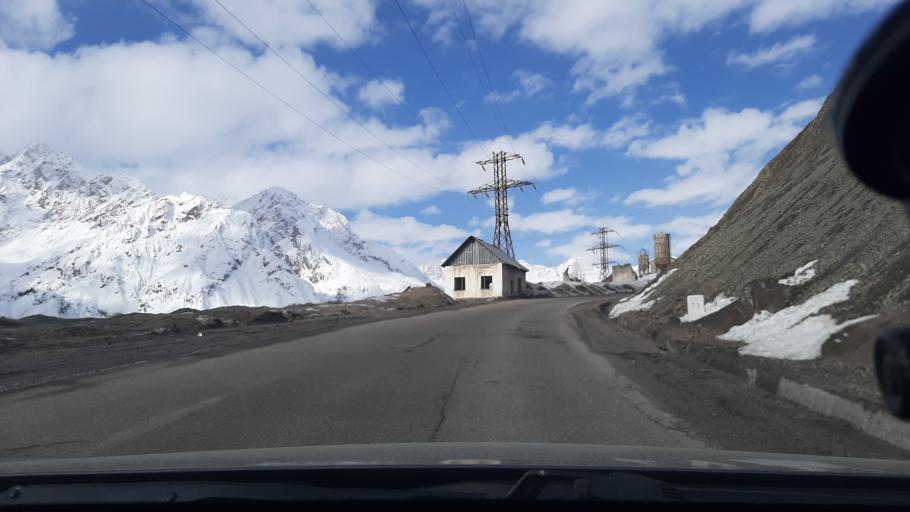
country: TJ
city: Tagob
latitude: 39.0591
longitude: 68.7030
